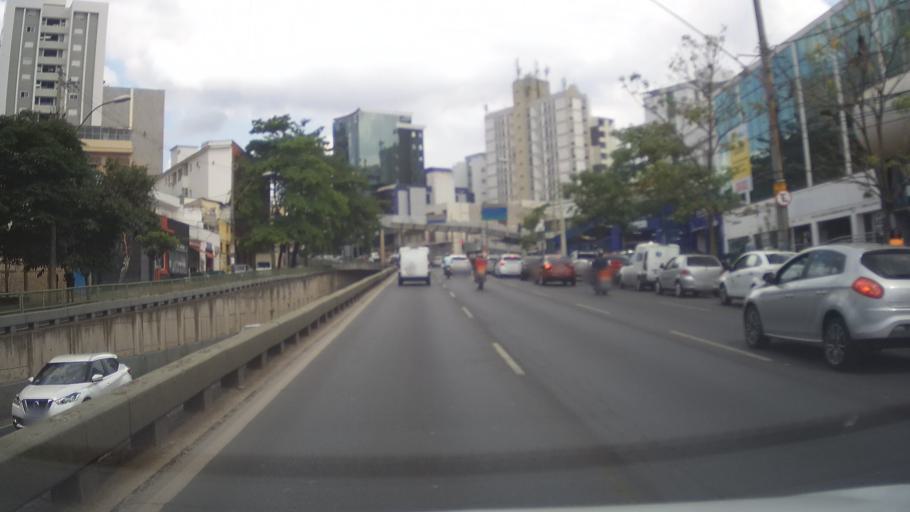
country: BR
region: Minas Gerais
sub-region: Belo Horizonte
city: Belo Horizonte
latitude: -19.9328
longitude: -43.9544
